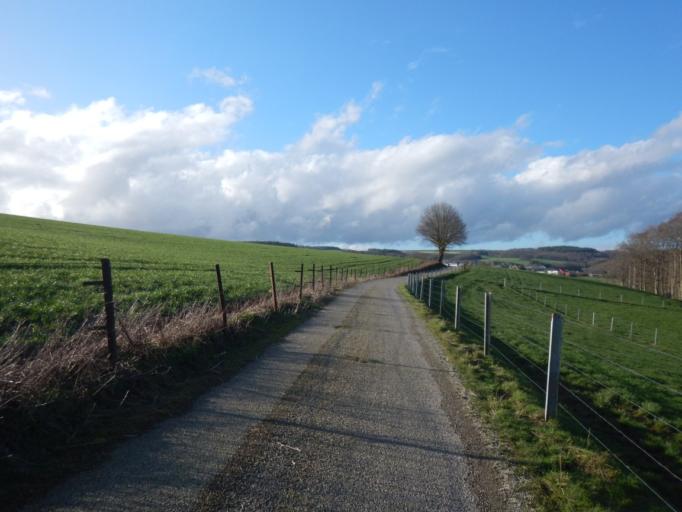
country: BE
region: Wallonia
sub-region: Province du Luxembourg
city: Attert
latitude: 49.7711
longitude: 5.8158
